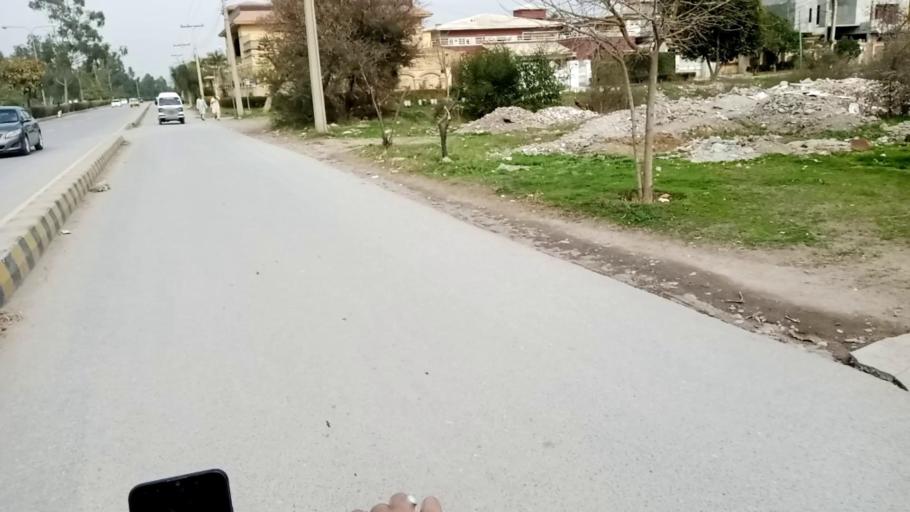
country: PK
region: Khyber Pakhtunkhwa
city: Peshawar
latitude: 33.9651
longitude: 71.4330
